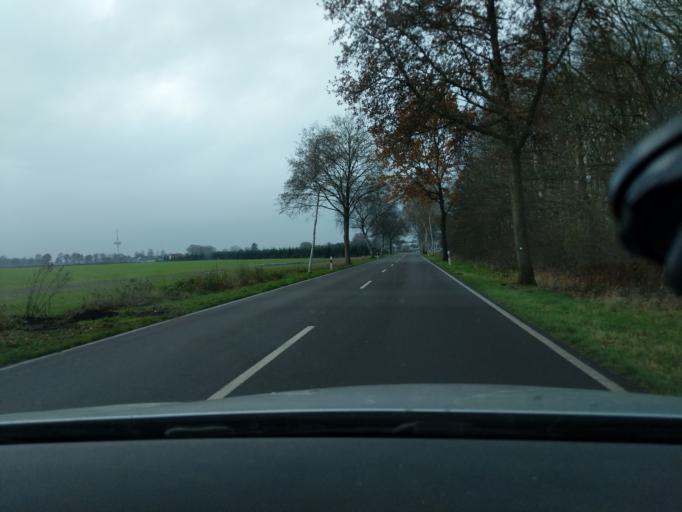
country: DE
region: Lower Saxony
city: Ahlerstedt
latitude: 53.3698
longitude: 9.4366
